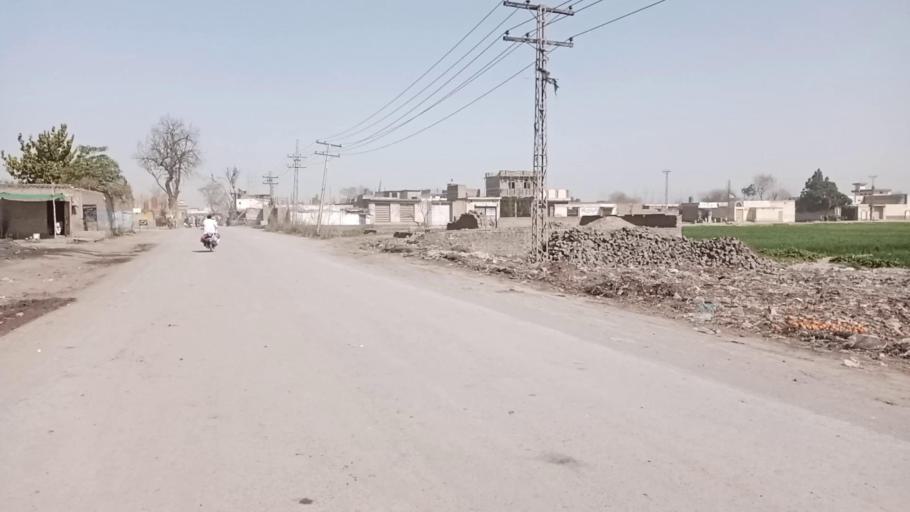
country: PK
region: Khyber Pakhtunkhwa
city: Peshawar
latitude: 33.9950
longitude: 71.6338
